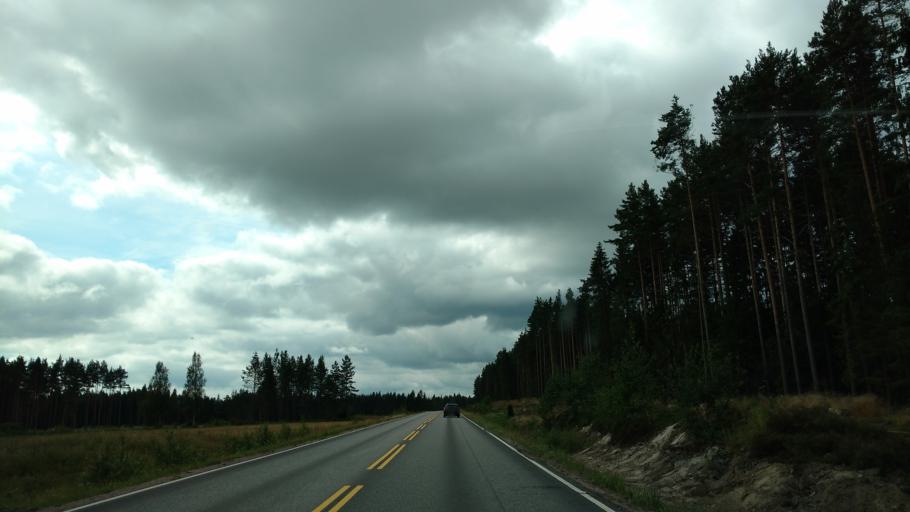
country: FI
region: Varsinais-Suomi
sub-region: Aboland-Turunmaa
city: Vaestanfjaerd
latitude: 60.1252
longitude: 22.6278
